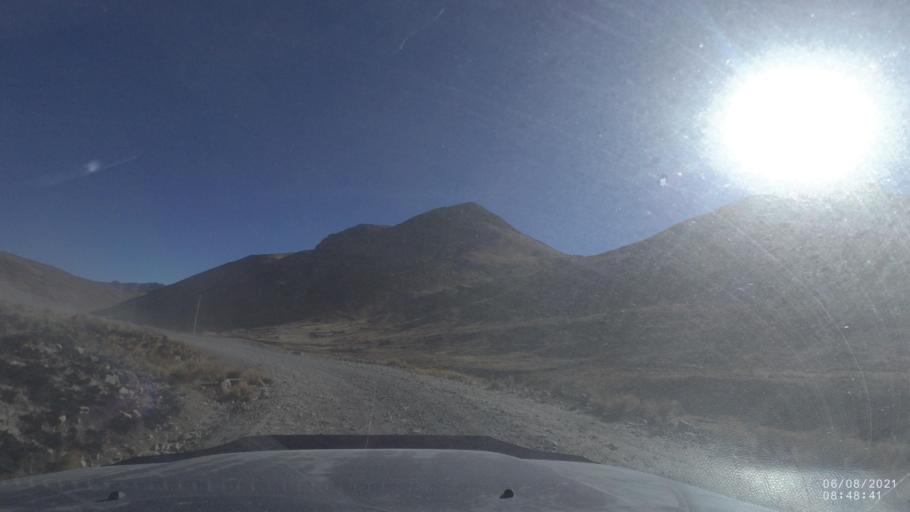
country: BO
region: Cochabamba
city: Sipe Sipe
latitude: -17.1611
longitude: -66.4303
